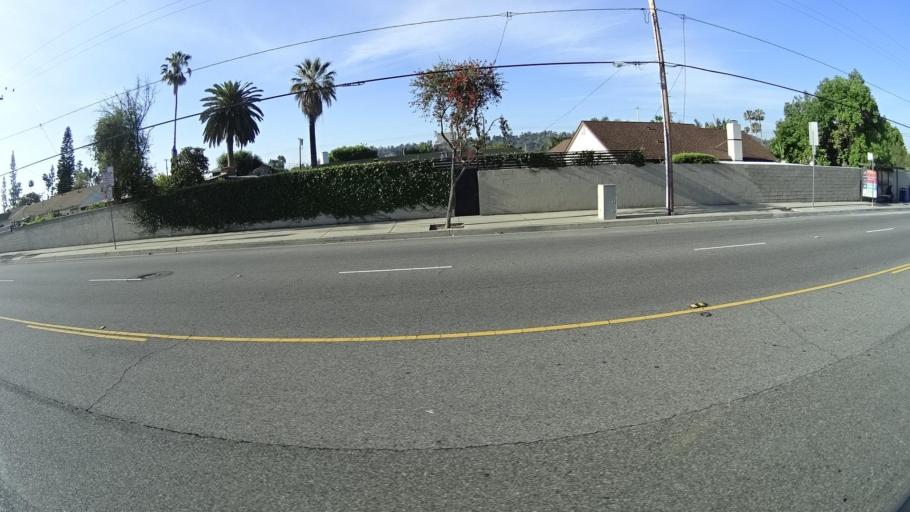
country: US
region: California
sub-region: Los Angeles County
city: Valinda
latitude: 34.0357
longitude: -117.9255
